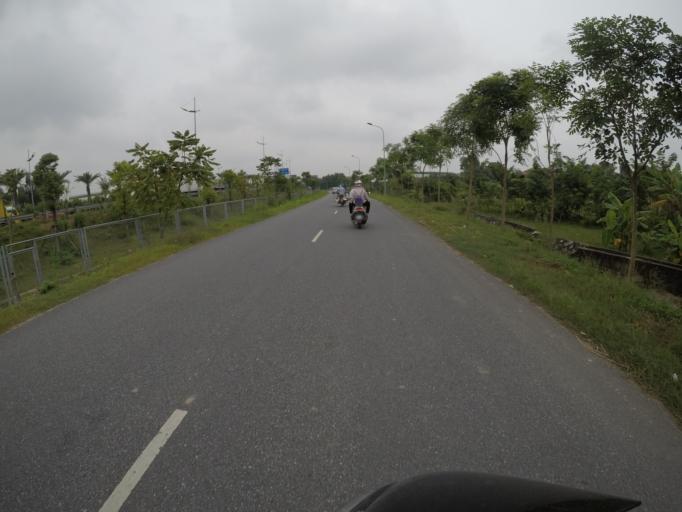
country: VN
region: Ha Noi
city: Dong Anh
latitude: 21.1952
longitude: 105.8355
